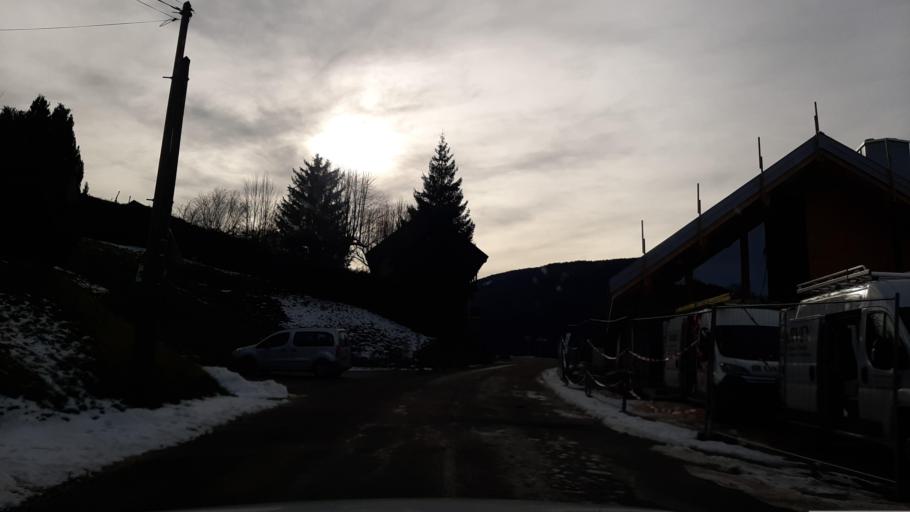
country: FR
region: Rhone-Alpes
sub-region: Departement de la Savoie
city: Cruet
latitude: 45.6511
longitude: 6.0942
